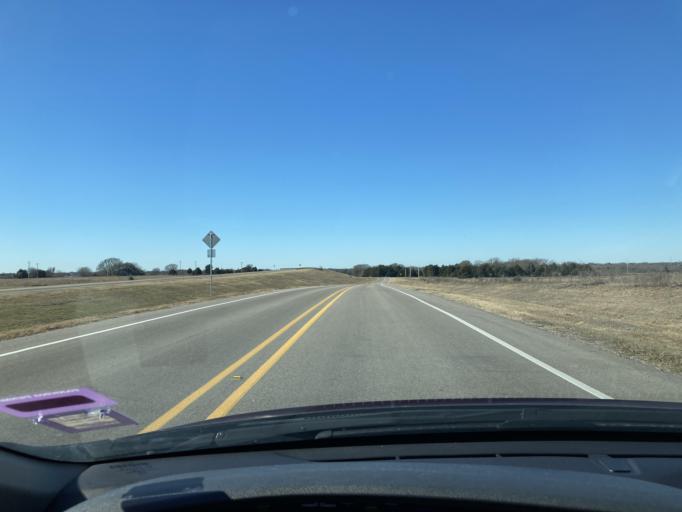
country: US
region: Texas
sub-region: Navarro County
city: Corsicana
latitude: 32.0483
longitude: -96.4919
